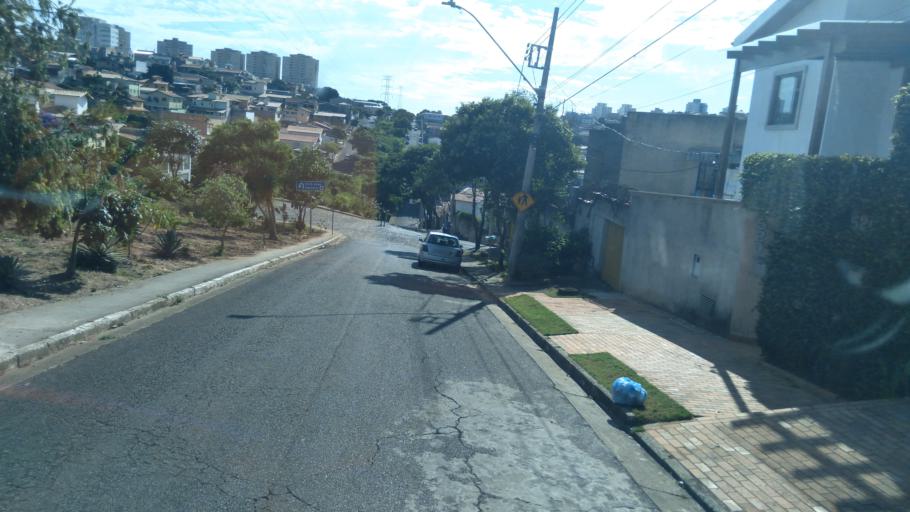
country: BR
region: Minas Gerais
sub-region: Belo Horizonte
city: Belo Horizonte
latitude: -19.8901
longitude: -43.8971
